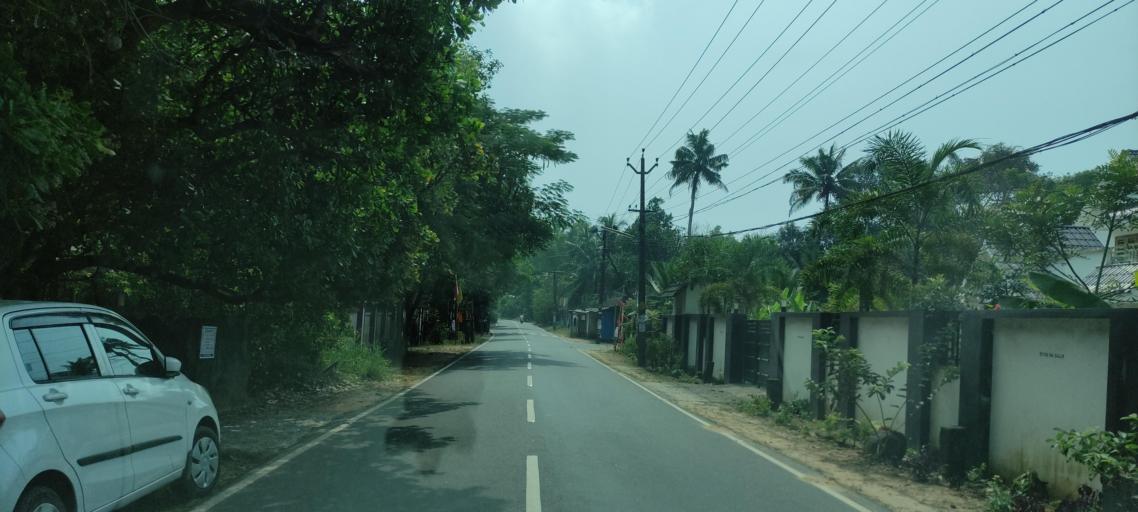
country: IN
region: Kerala
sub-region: Alappuzha
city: Alleppey
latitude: 9.5604
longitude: 76.3341
